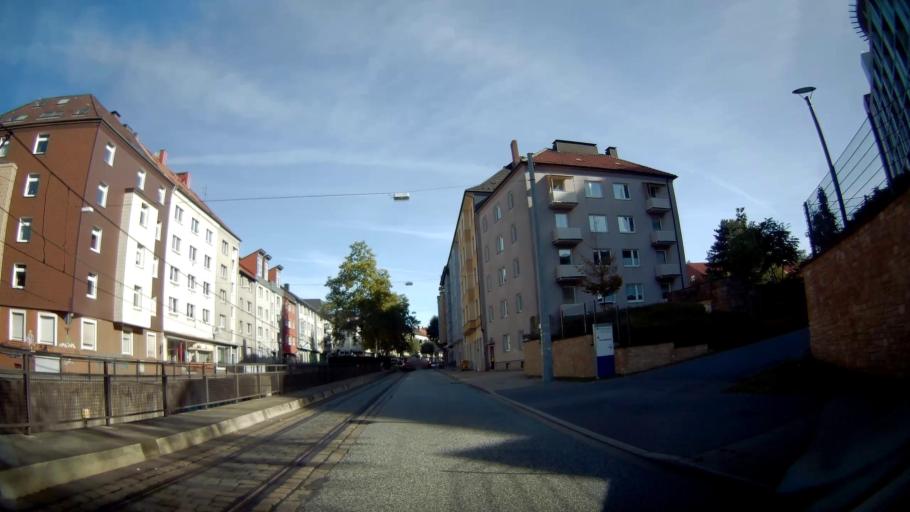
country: DE
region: North Rhine-Westphalia
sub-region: Regierungsbezirk Arnsberg
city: Bochum
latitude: 51.4694
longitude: 7.2096
